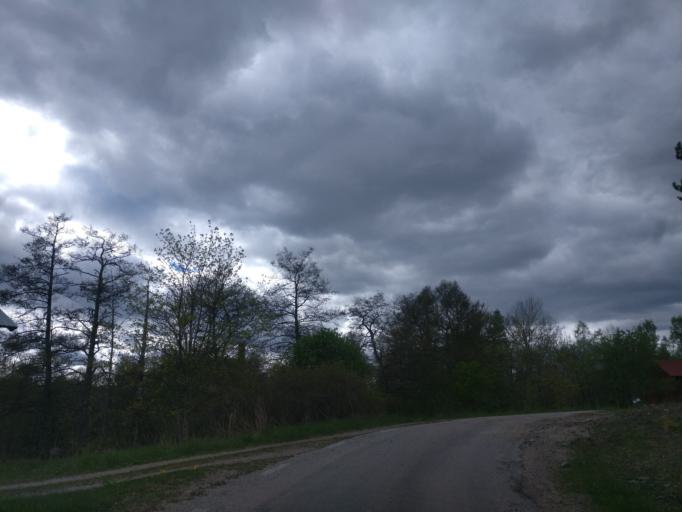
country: SE
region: Gaevleborg
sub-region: Soderhamns Kommun
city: Marielund
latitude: 61.4601
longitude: 17.1325
